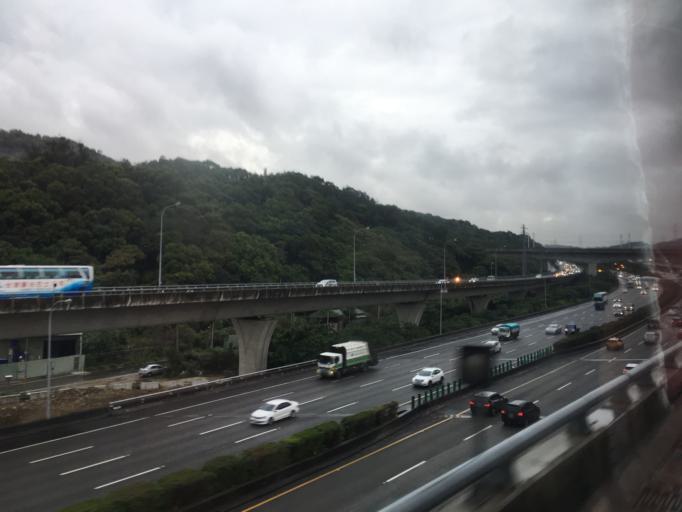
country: TW
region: Taiwan
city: Taoyuan City
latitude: 25.0475
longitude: 121.3177
